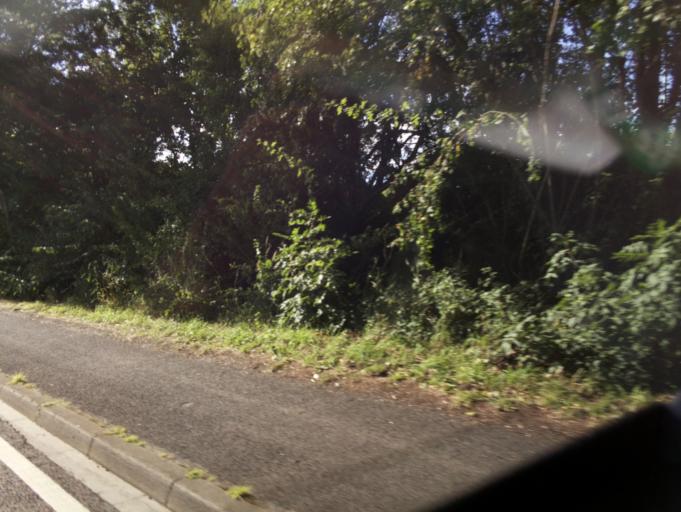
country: GB
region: England
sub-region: Hampshire
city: Romsey
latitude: 50.9865
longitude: -1.4682
